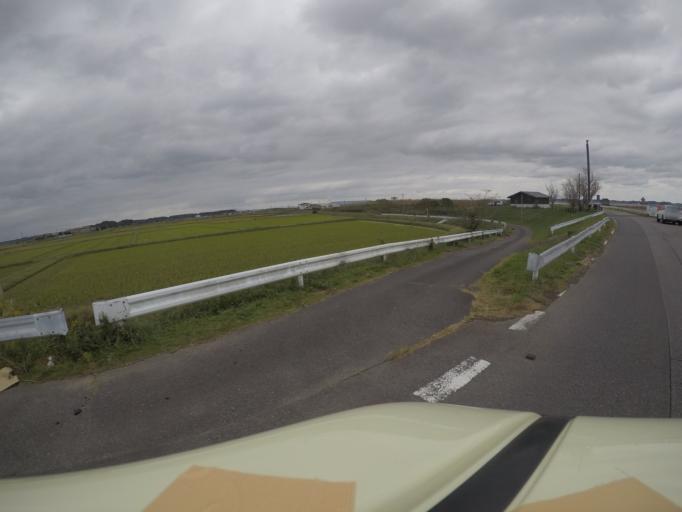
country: JP
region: Chiba
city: Katori-shi
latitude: 35.9602
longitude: 140.4580
